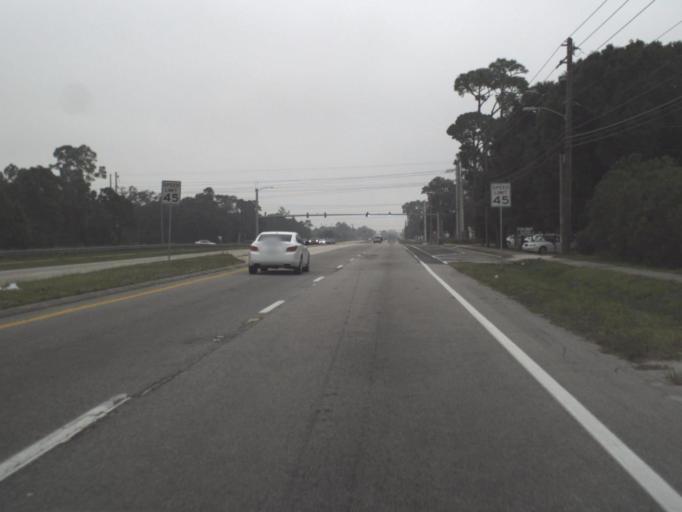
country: US
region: Florida
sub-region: Brevard County
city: June Park
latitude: 28.0456
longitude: -80.6714
